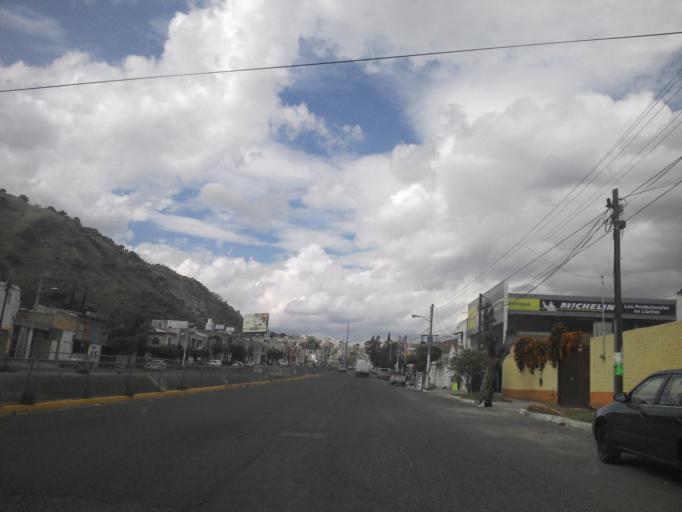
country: MX
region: Jalisco
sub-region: Tlajomulco de Zuniga
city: Palomar
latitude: 20.6533
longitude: -103.4519
